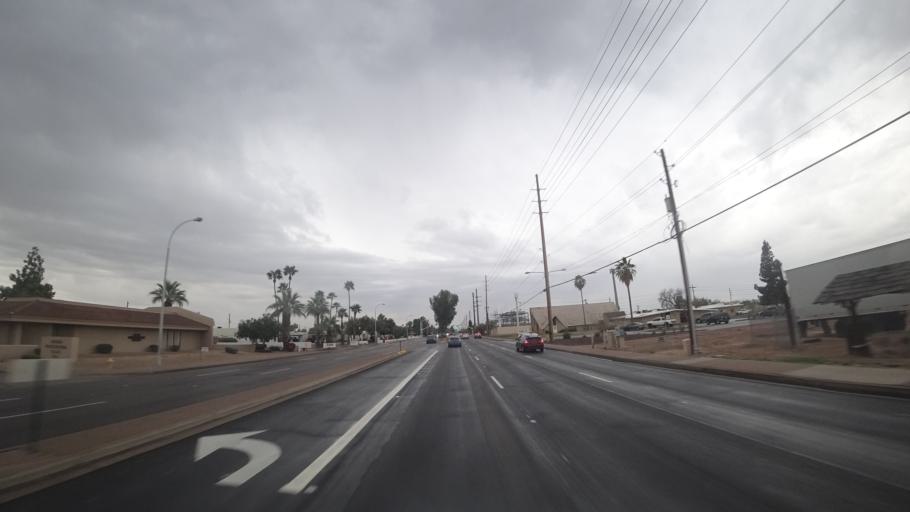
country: US
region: Arizona
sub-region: Maricopa County
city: Scottsdale
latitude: 33.4752
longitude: -111.9090
